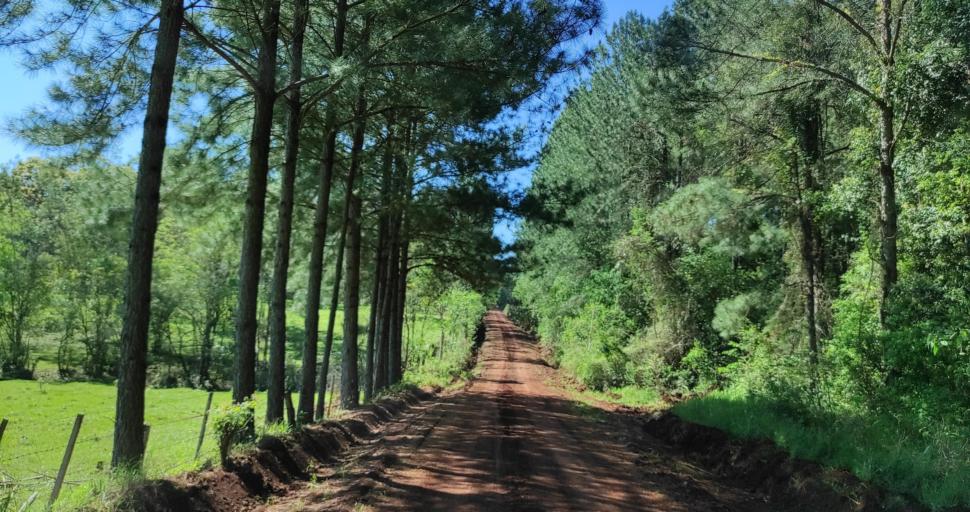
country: AR
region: Misiones
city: Ruiz de Montoya
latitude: -26.9491
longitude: -55.0031
